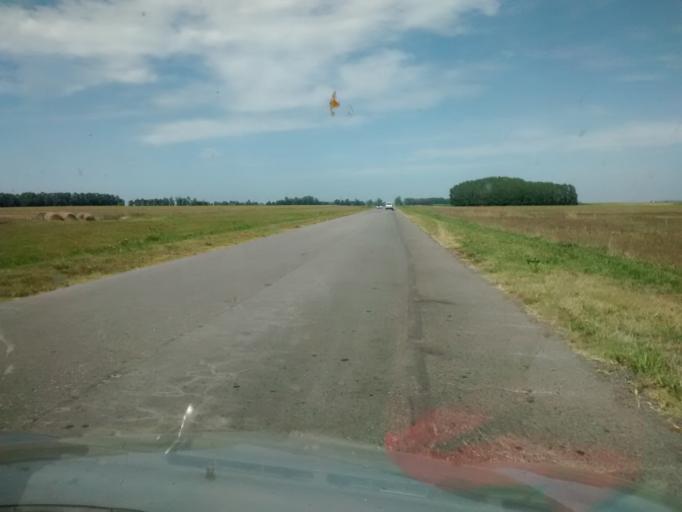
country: AR
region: Buenos Aires
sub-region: Partido de Ayacucho
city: Ayacucho
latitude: -37.1951
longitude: -58.5089
